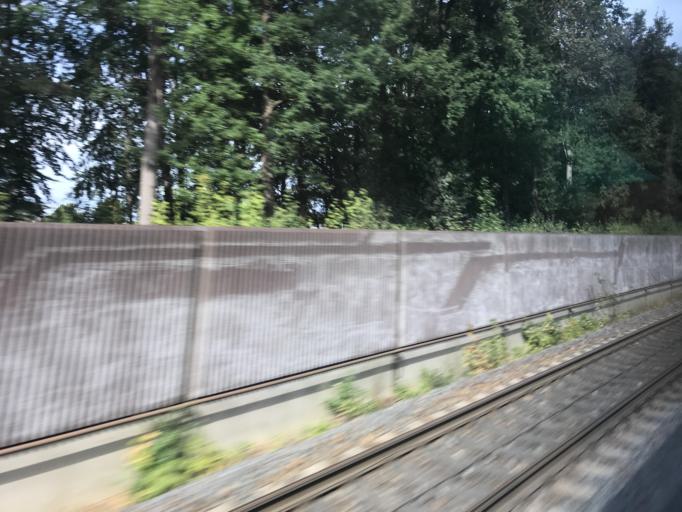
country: DE
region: North Rhine-Westphalia
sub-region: Regierungsbezirk Koln
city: Mengenich
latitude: 50.9459
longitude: 6.8613
